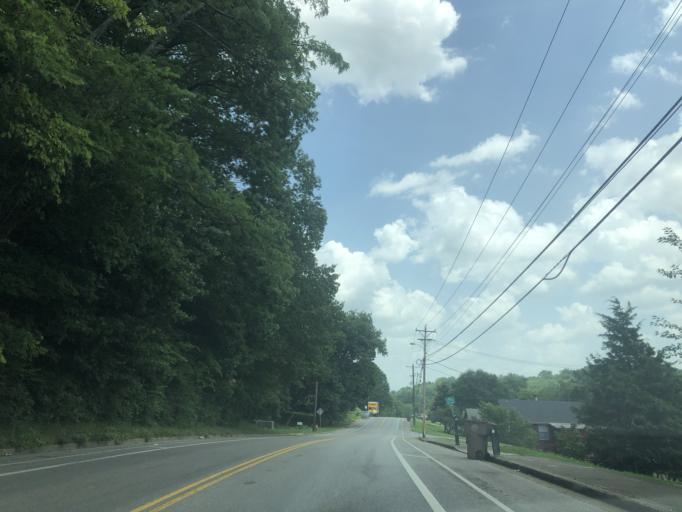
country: US
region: Tennessee
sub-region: Williamson County
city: Brentwood Estates
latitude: 36.0529
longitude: -86.6885
